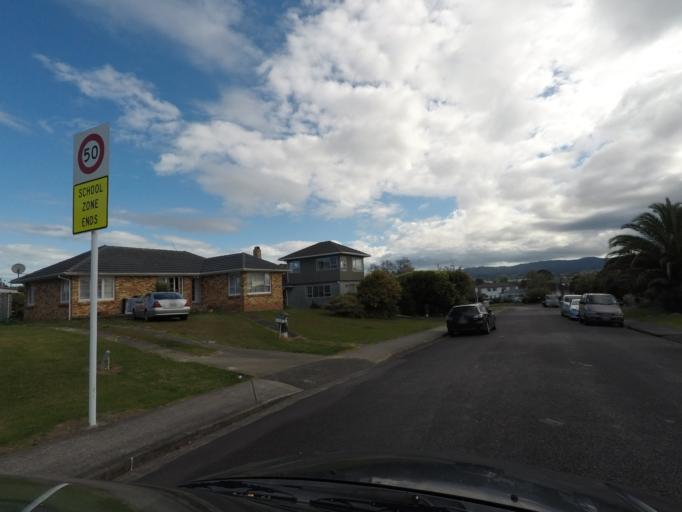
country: NZ
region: Auckland
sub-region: Auckland
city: Rosebank
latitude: -36.8703
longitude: 174.6448
